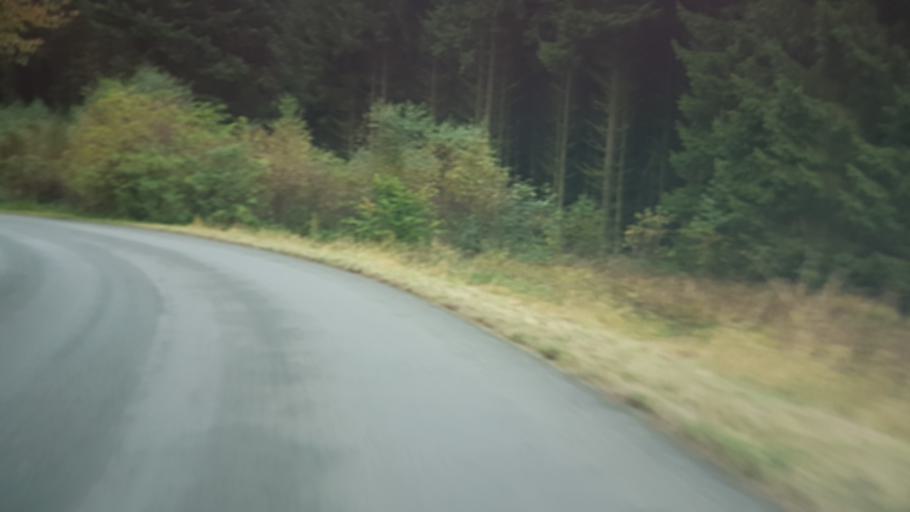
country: DE
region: North Rhine-Westphalia
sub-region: Regierungsbezirk Arnsberg
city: Luedenscheid
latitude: 51.2173
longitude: 7.6744
